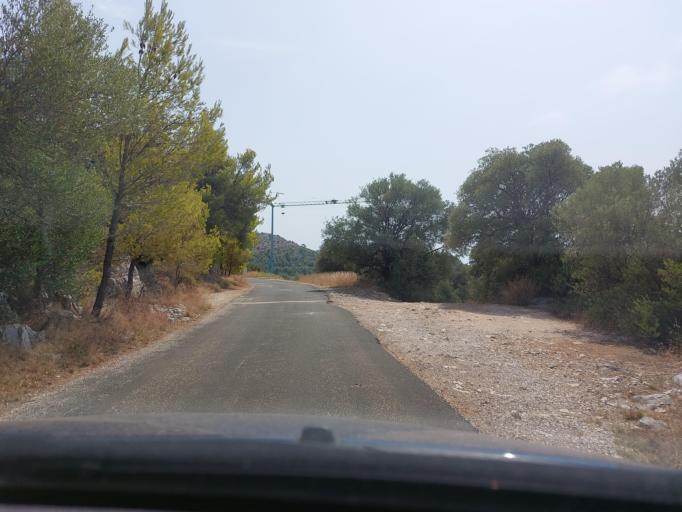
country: HR
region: Dubrovacko-Neretvanska
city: Smokvica
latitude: 42.7363
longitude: 16.8894
